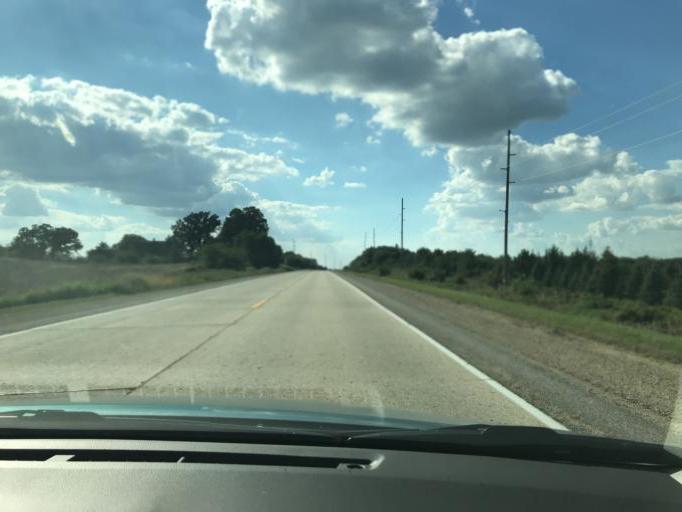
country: US
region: Wisconsin
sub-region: Rock County
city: Orfordville
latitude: 42.5574
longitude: -89.2981
